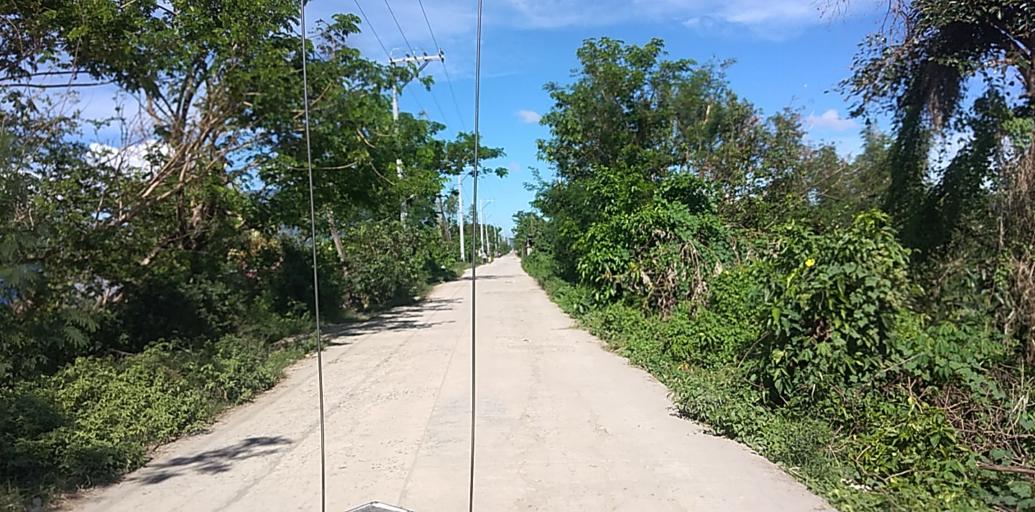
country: PH
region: Central Luzon
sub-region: Province of Pampanga
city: Candating
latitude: 15.1238
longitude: 120.8120
